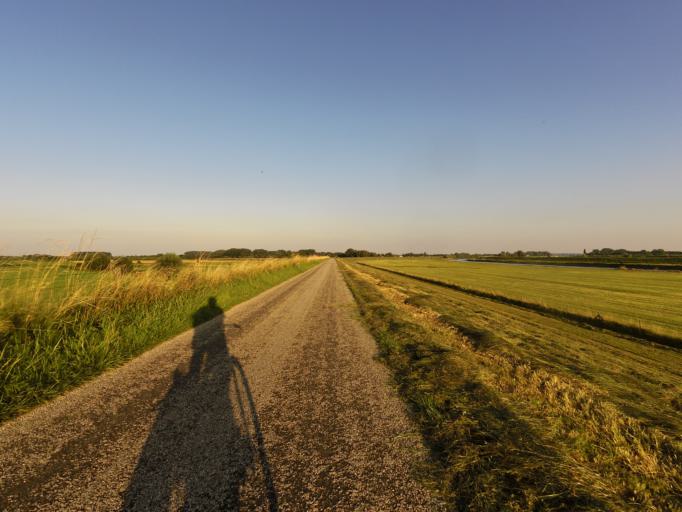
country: NL
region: Gelderland
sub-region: Gemeente Duiven
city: Duiven
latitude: 51.9068
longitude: 6.0111
